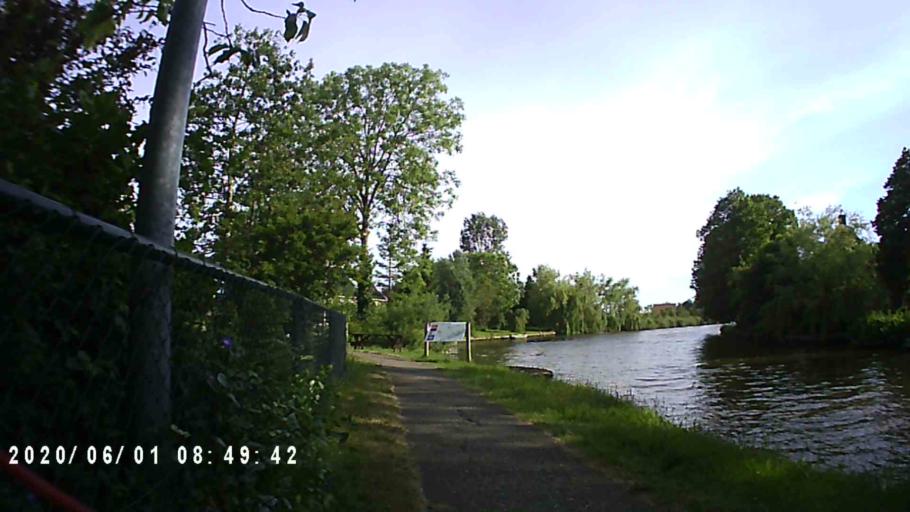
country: NL
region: Friesland
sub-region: Gemeente Ferwerderadiel
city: Burdaard
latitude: 53.2752
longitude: 5.8387
